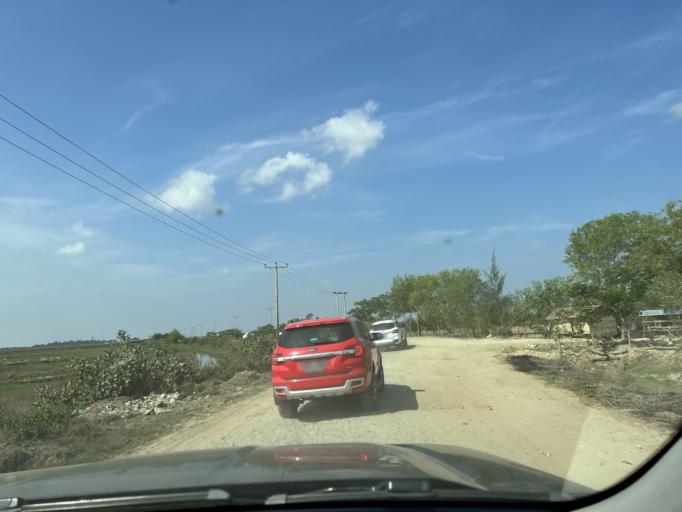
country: MM
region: Ayeyarwady
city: Pyapon
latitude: 16.0130
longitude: 95.6031
